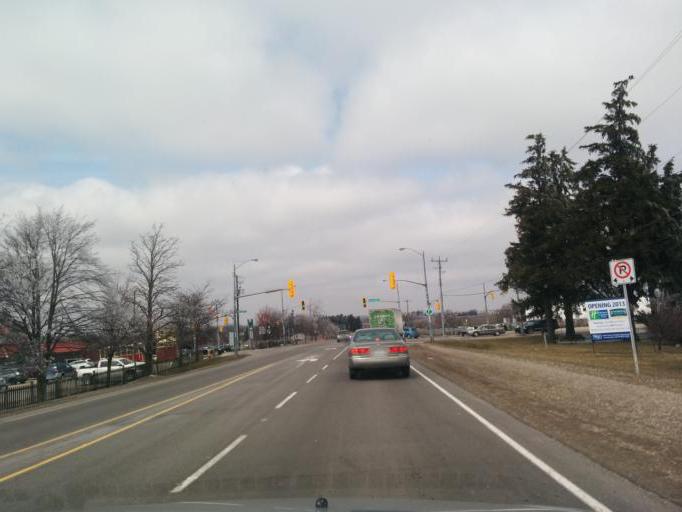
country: CA
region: Ontario
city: Waterloo
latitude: 43.5092
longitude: -80.5567
